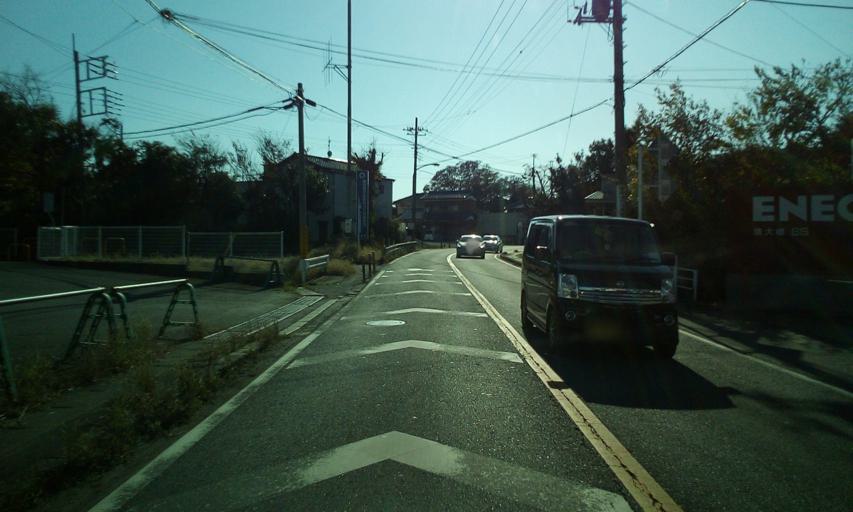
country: JP
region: Ibaraki
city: Sakai
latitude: 36.0931
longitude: 139.7887
